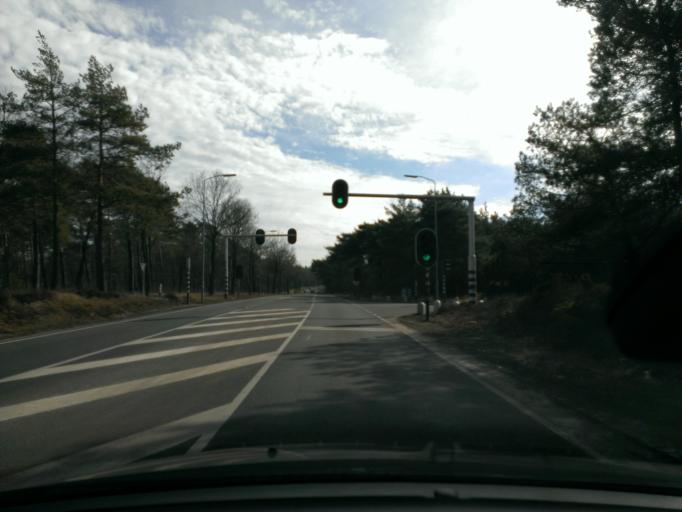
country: NL
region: Gelderland
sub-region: Gemeente Hattem
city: Hattem
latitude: 52.4471
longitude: 6.0082
